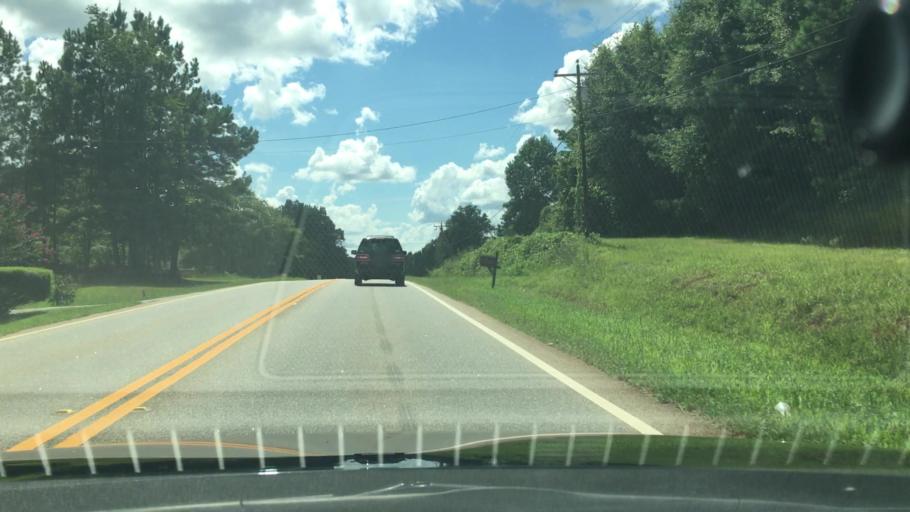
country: US
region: Georgia
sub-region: Putnam County
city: Eatonton
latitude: 33.3162
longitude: -83.4282
